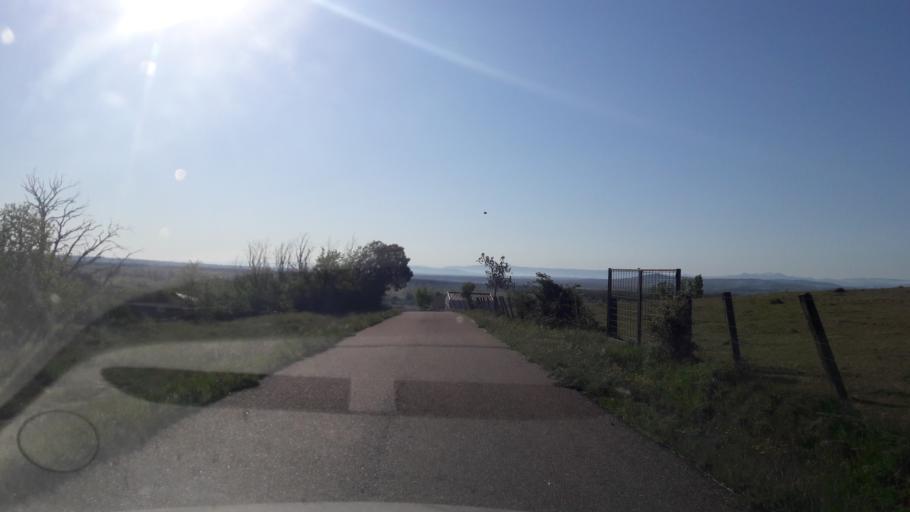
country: ES
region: Castille and Leon
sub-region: Provincia de Salamanca
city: Herguijuela del Campo
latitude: 40.6296
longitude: -5.8659
